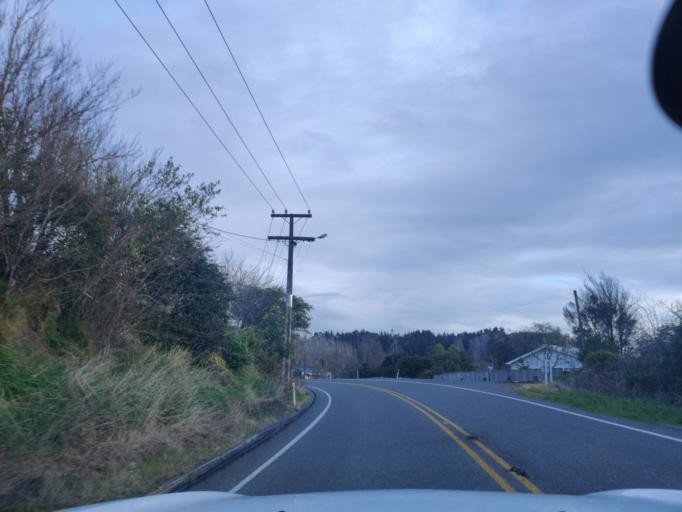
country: NZ
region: Manawatu-Wanganui
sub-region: Palmerston North City
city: Palmerston North
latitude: -40.3733
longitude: 175.6516
